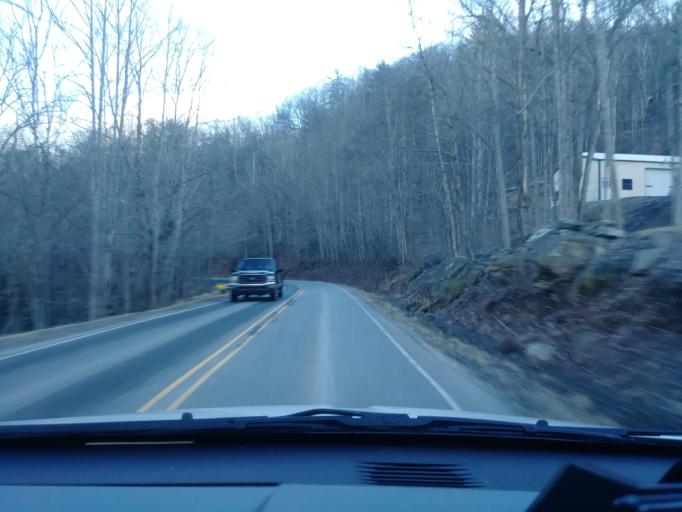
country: US
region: North Carolina
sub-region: Avery County
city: Newland
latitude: 36.1638
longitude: -81.9549
